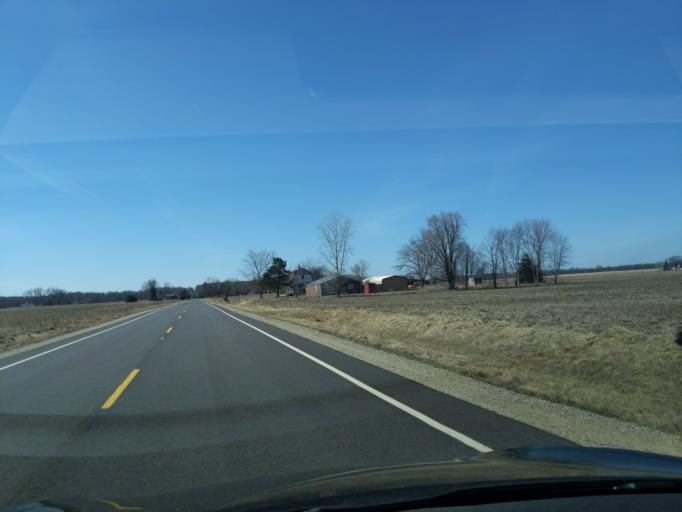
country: US
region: Michigan
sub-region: Ionia County
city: Lake Odessa
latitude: 42.7270
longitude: -85.0265
